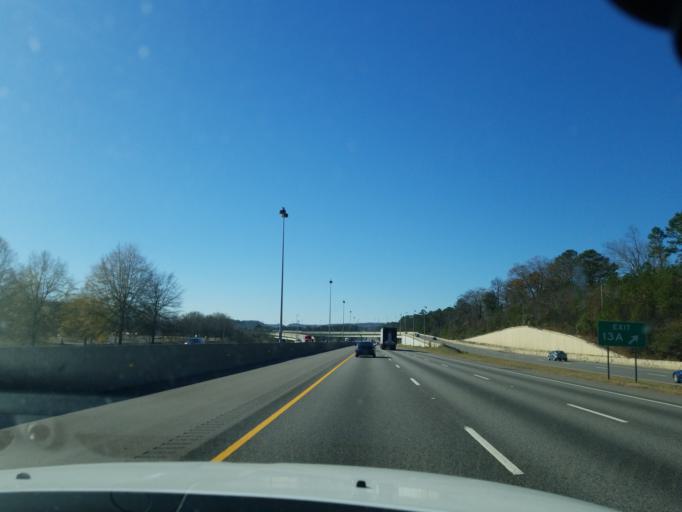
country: US
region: Alabama
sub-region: Jefferson County
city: Hoover
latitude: 33.3838
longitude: -86.8085
